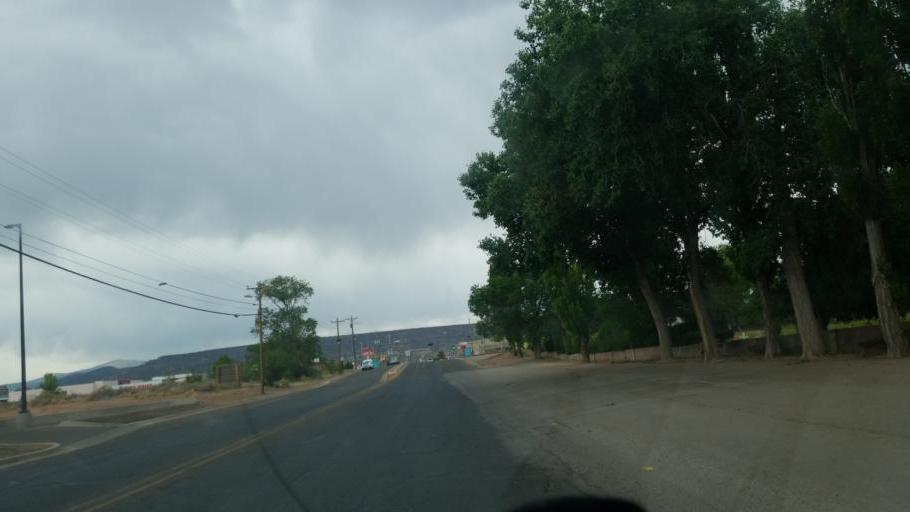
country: US
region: New Mexico
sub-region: Cibola County
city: Grants
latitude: 35.1611
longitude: -107.8363
